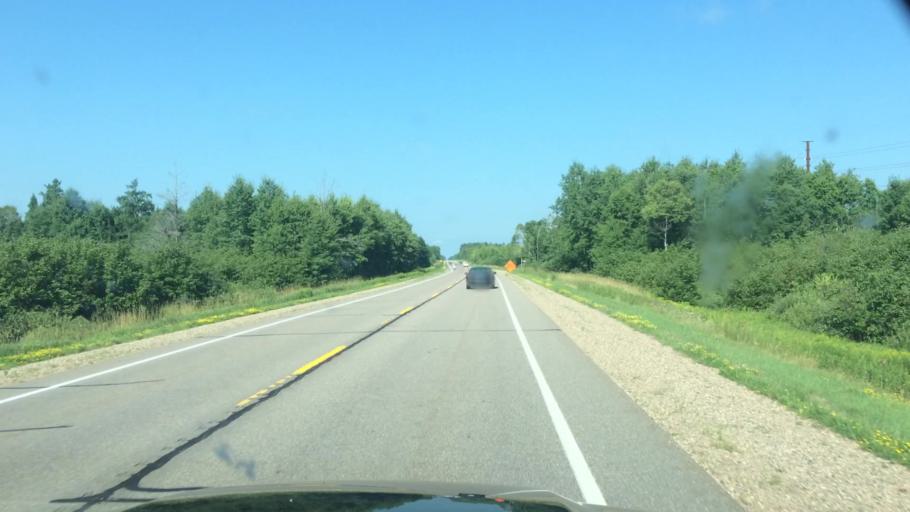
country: US
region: Wisconsin
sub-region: Langlade County
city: Antigo
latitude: 45.1467
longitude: -89.3419
